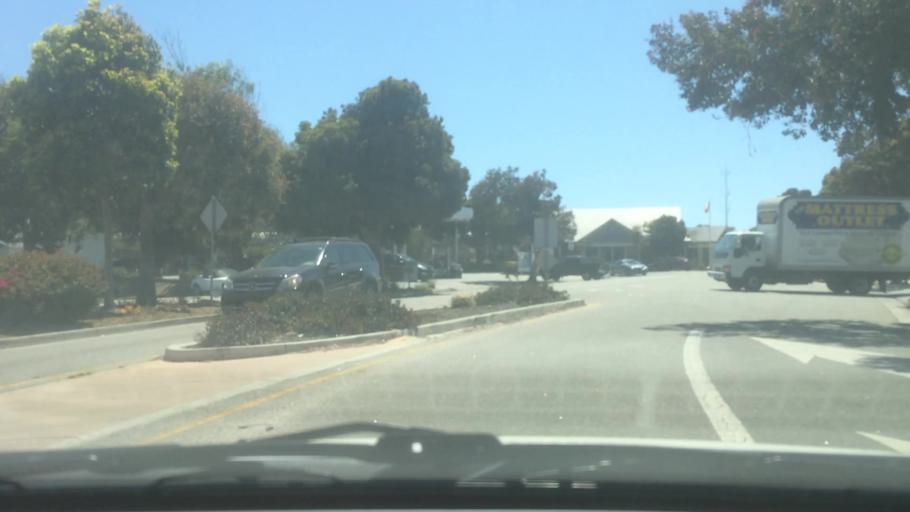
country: US
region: California
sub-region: San Luis Obispo County
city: Morro Bay
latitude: 35.3664
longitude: -120.8414
